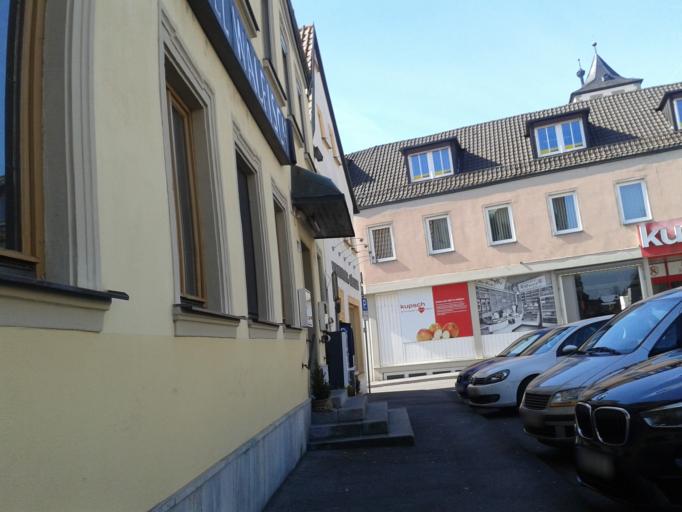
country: DE
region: Bavaria
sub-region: Regierungsbezirk Unterfranken
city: Hassfurt
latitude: 50.0314
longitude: 10.5108
